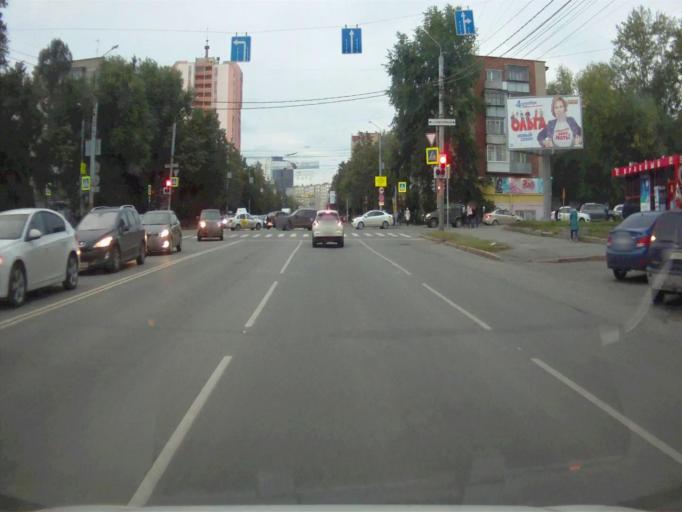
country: RU
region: Chelyabinsk
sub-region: Gorod Chelyabinsk
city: Chelyabinsk
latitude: 55.1586
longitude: 61.3810
